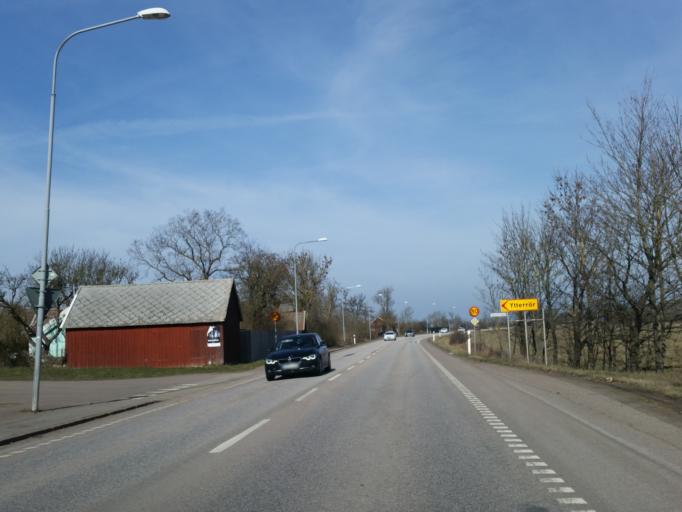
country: SE
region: Kalmar
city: Faerjestaden
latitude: 56.7207
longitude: 16.5363
